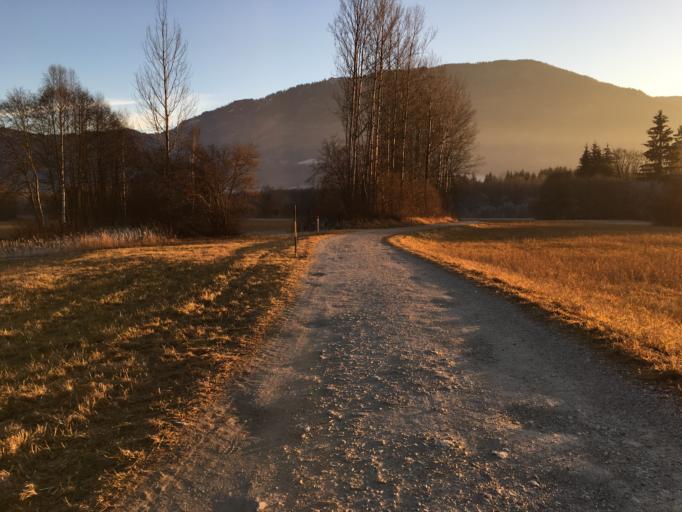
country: AT
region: Styria
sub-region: Politischer Bezirk Liezen
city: Weissenbach bei Liezen
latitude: 47.5625
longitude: 14.1956
